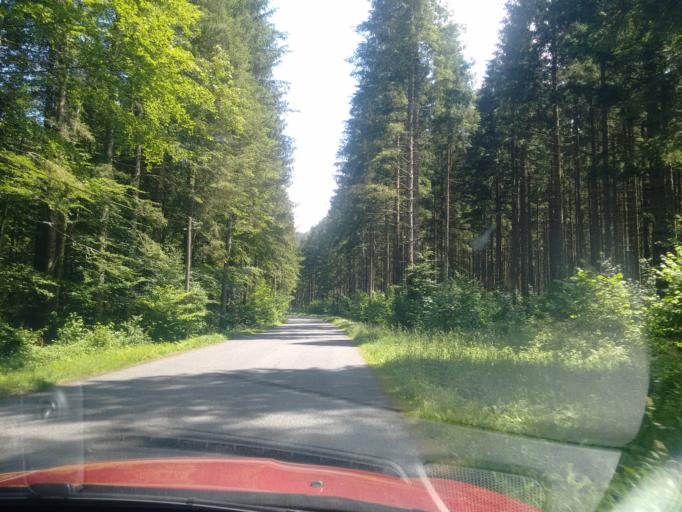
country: AT
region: Upper Austria
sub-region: Politischer Bezirk Gmunden
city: Ebensee
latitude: 47.8356
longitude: 13.6958
